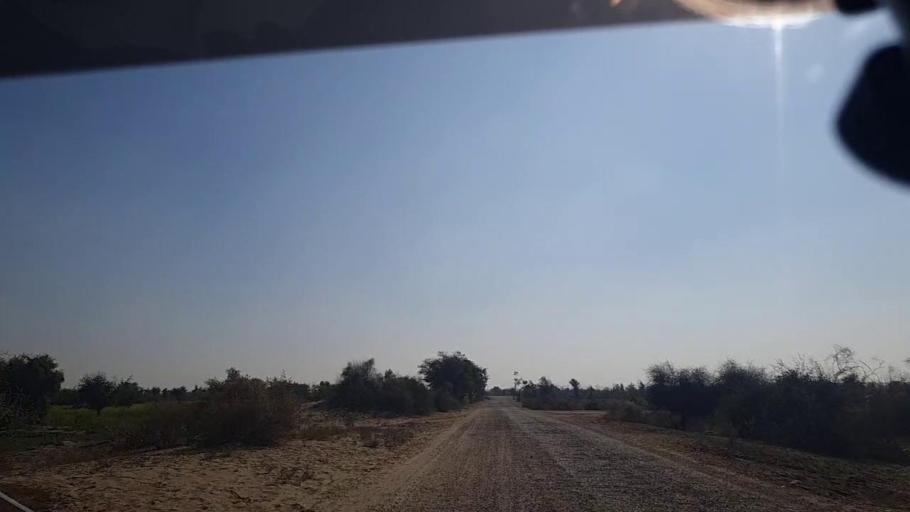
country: PK
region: Sindh
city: Khanpur
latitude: 27.5674
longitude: 69.3046
